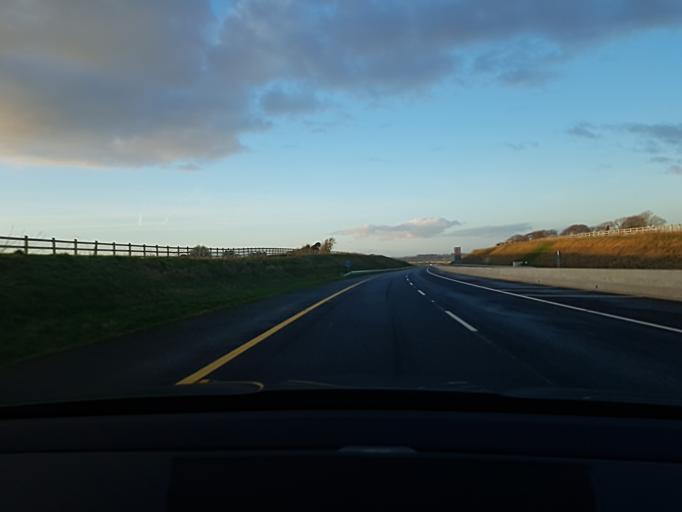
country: IE
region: Connaught
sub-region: County Galway
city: Tuam
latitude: 53.4082
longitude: -8.8254
